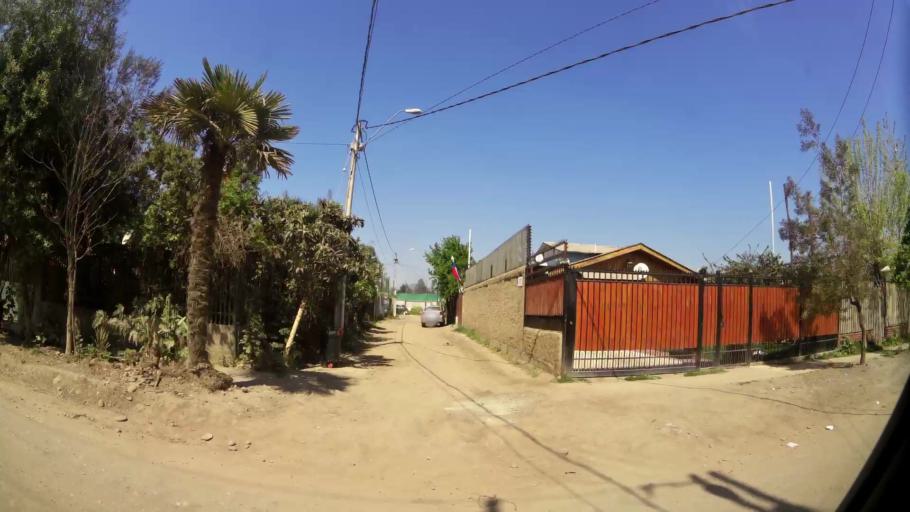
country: CL
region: Santiago Metropolitan
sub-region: Provincia de Talagante
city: Penaflor
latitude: -33.5851
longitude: -70.8101
